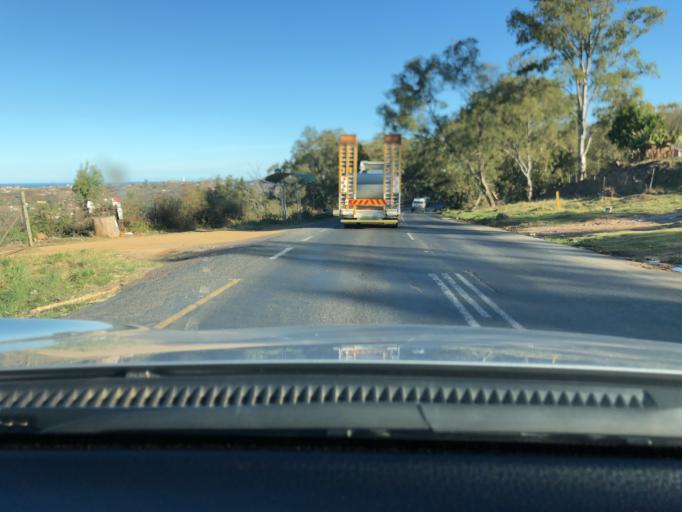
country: ZA
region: KwaZulu-Natal
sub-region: eThekwini Metropolitan Municipality
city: Umkomaas
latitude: -30.0258
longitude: 30.8122
